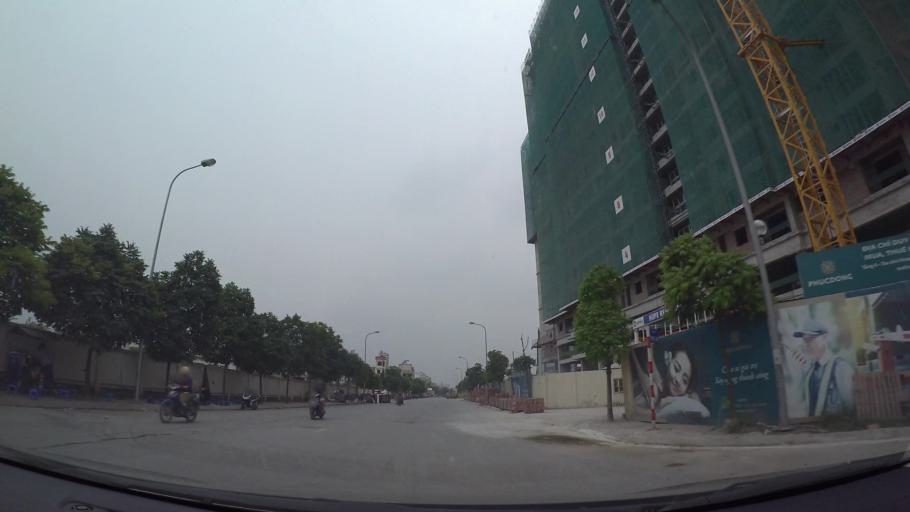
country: VN
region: Ha Noi
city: Trau Quy
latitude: 21.0412
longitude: 105.9042
